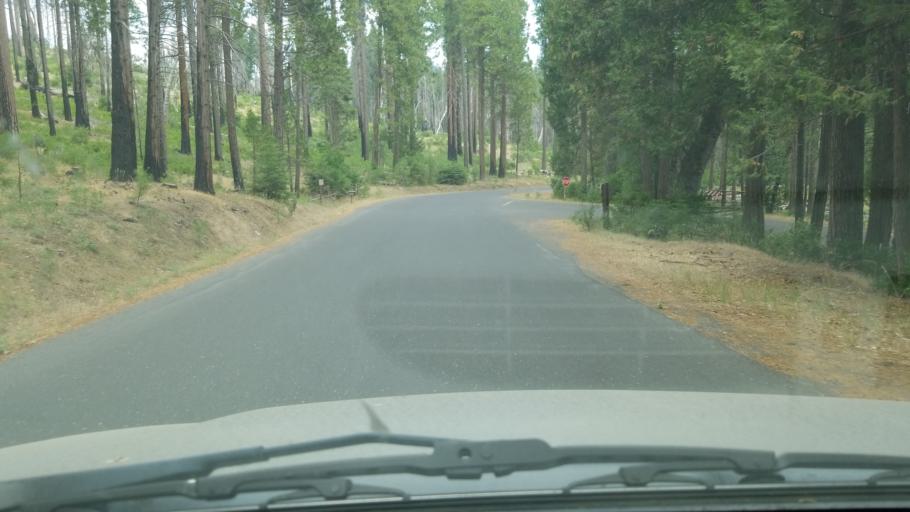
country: US
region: California
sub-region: Mariposa County
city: Yosemite Valley
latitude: 37.8638
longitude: -119.8692
